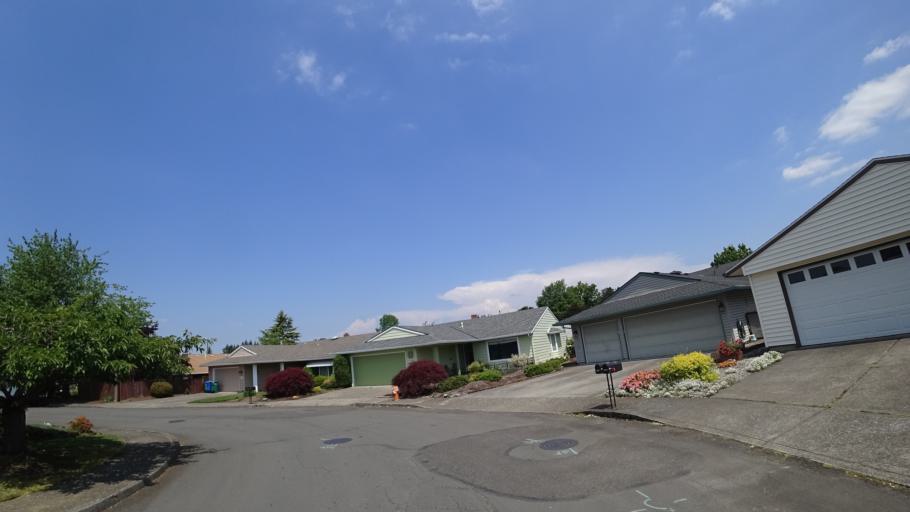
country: US
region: Oregon
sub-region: Multnomah County
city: Fairview
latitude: 45.5378
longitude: -122.5081
